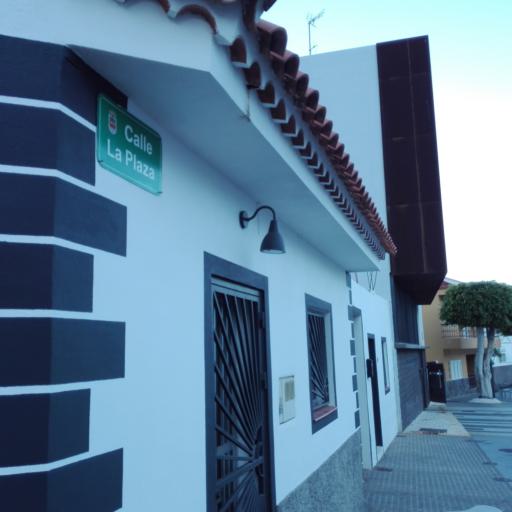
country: ES
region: Canary Islands
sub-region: Provincia de Santa Cruz de Tenerife
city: Candelaria
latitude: 28.4022
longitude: -16.3610
